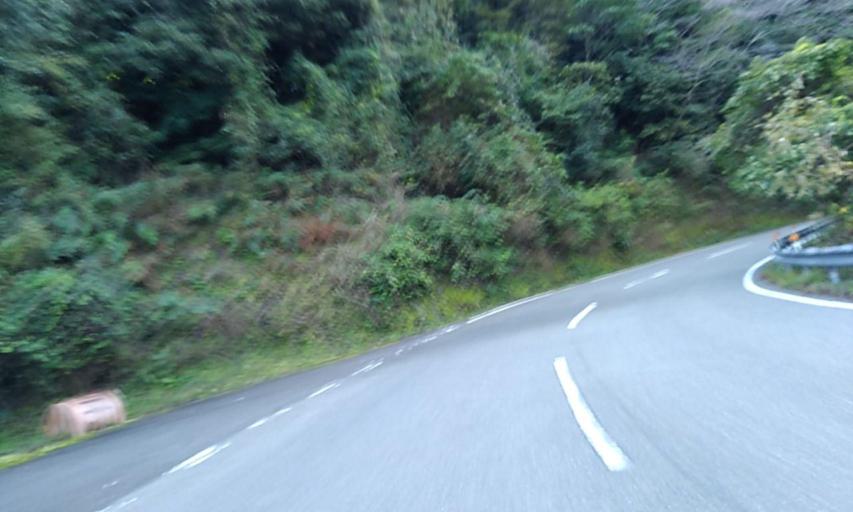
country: JP
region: Wakayama
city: Iwade
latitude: 34.1147
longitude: 135.3461
